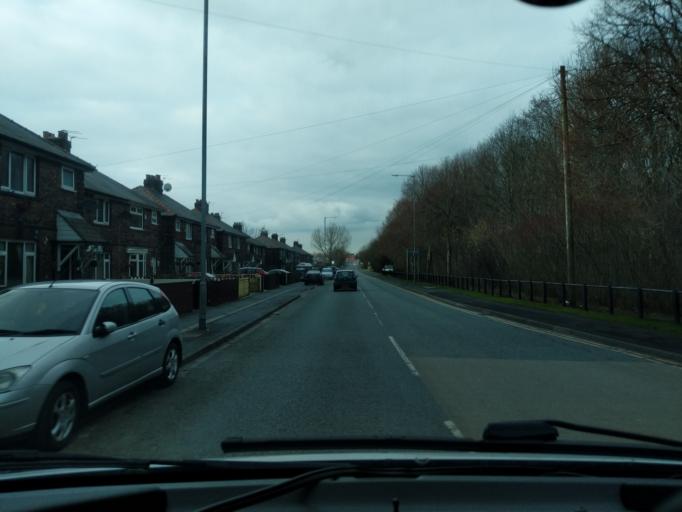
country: GB
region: England
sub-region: St. Helens
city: St Helens
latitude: 53.4445
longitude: -2.7185
